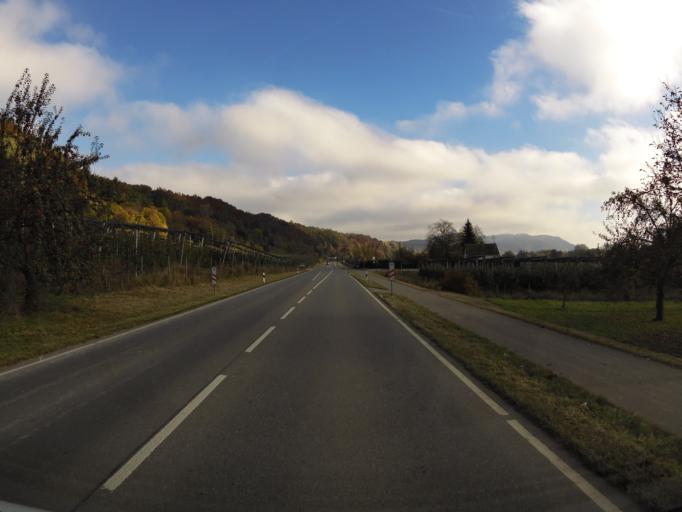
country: DE
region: Baden-Wuerttemberg
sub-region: Freiburg Region
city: Bodman-Ludwigshafen
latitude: 47.8179
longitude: 9.0239
